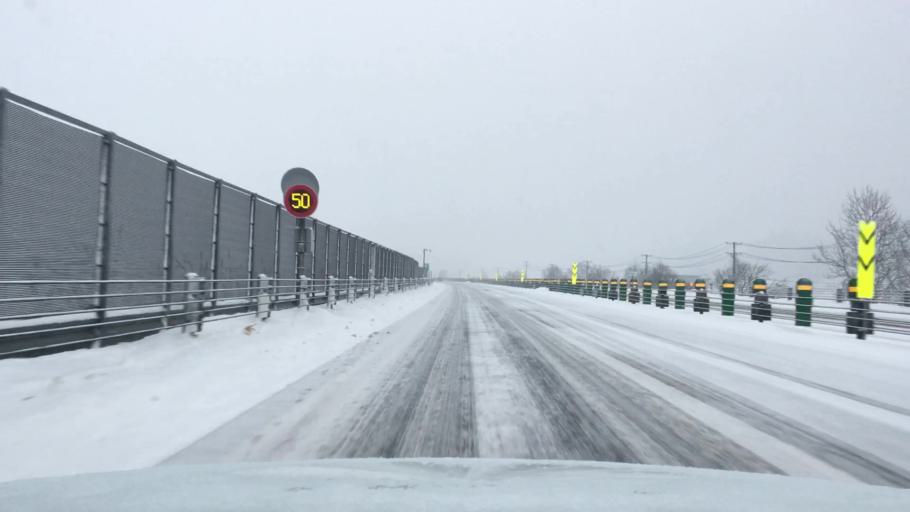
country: JP
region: Akita
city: Hanawa
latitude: 40.2870
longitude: 140.7593
